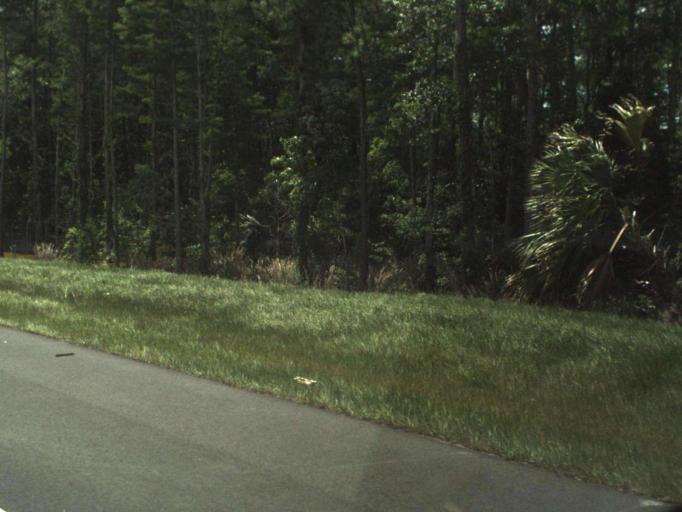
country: US
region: Florida
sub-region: Volusia County
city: Lake Helen
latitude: 29.0569
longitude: -81.1948
